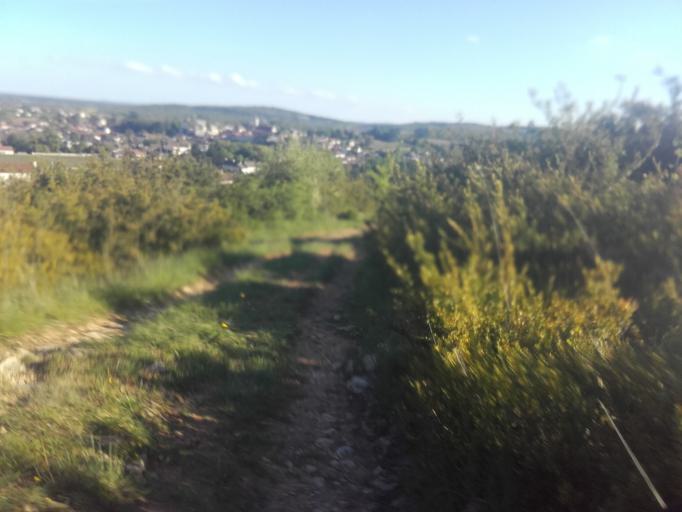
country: FR
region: Bourgogne
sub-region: Departement de Saone-et-Loire
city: Rully
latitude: 46.8829
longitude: 4.7379
